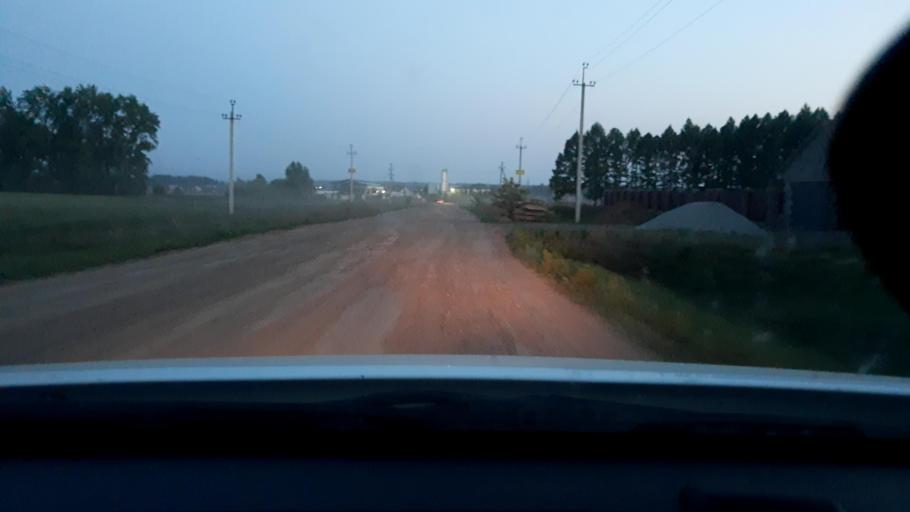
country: RU
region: Bashkortostan
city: Avdon
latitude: 54.5144
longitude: 55.8221
